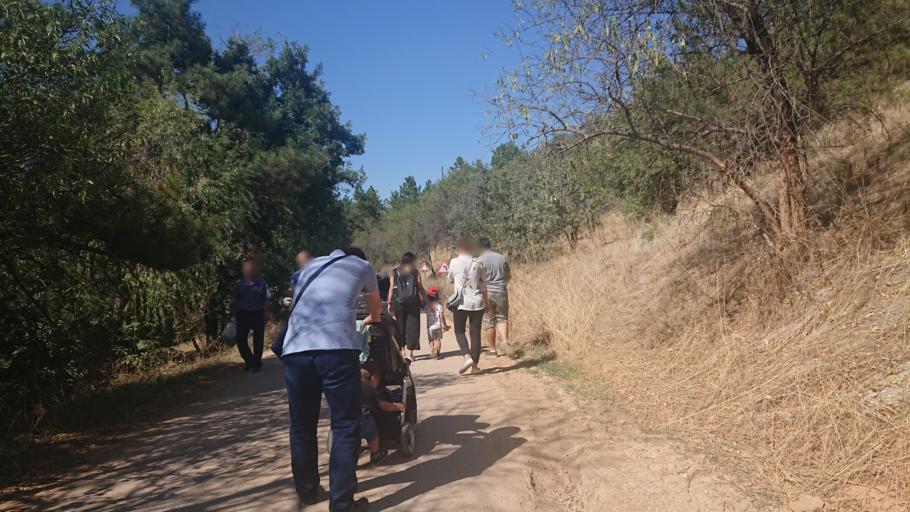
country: TR
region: Ankara
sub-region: Goelbasi
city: Golbasi
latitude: 39.8143
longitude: 32.8214
